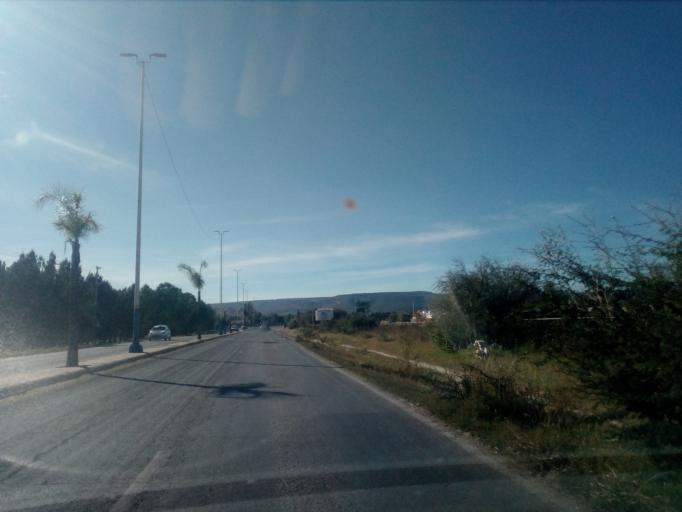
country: MX
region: Durango
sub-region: Durango
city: Sebastian Lerdo de Tejada
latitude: 23.9795
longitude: -104.6643
